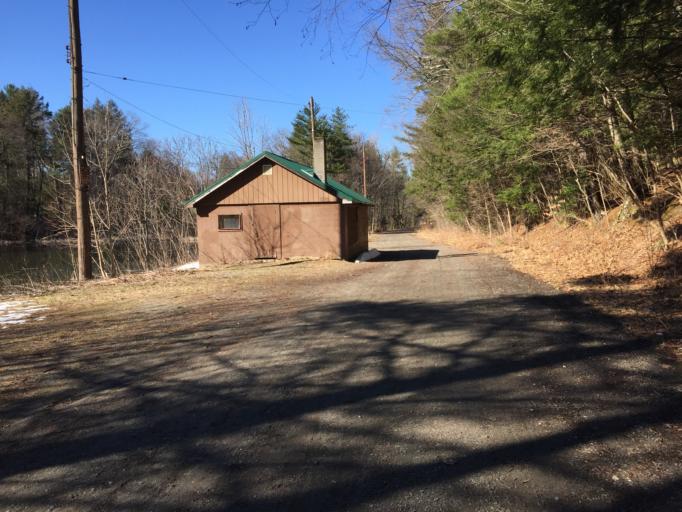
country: US
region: Massachusetts
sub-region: Franklin County
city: Greenfield
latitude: 42.5829
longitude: -72.5900
